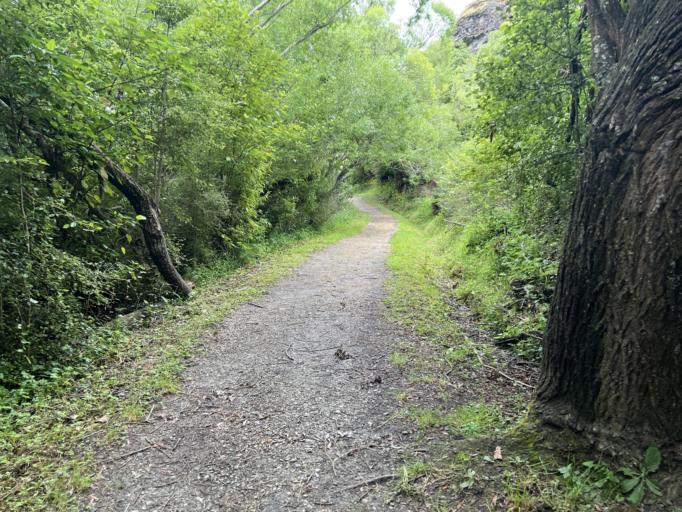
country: NZ
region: Otago
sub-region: Queenstown-Lakes District
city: Wanaka
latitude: -44.6469
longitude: 168.9627
